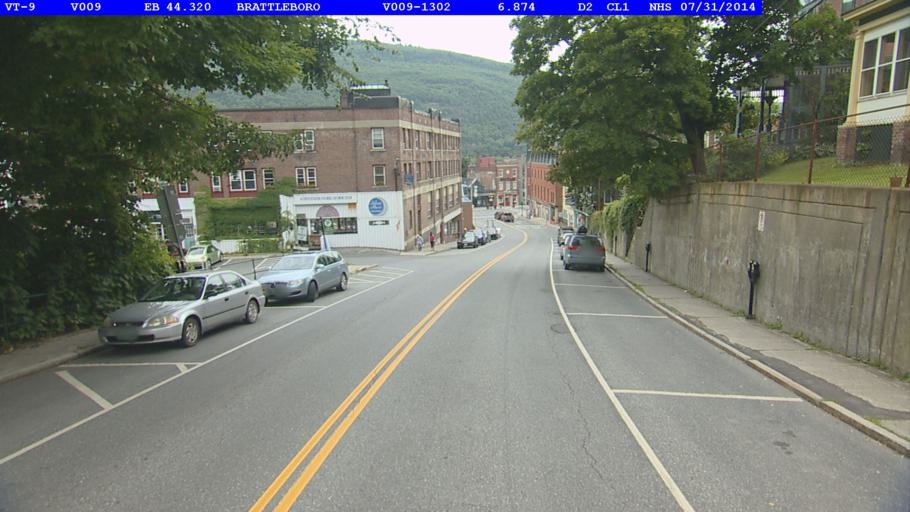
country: US
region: Vermont
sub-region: Windham County
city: Brattleboro
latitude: 42.8534
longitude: -72.5604
